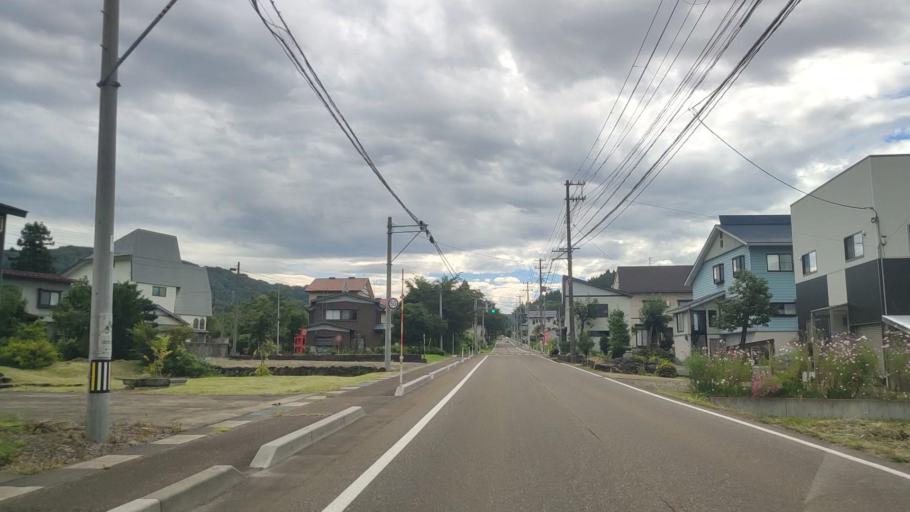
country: JP
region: Niigata
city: Arai
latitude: 37.0016
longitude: 138.2645
